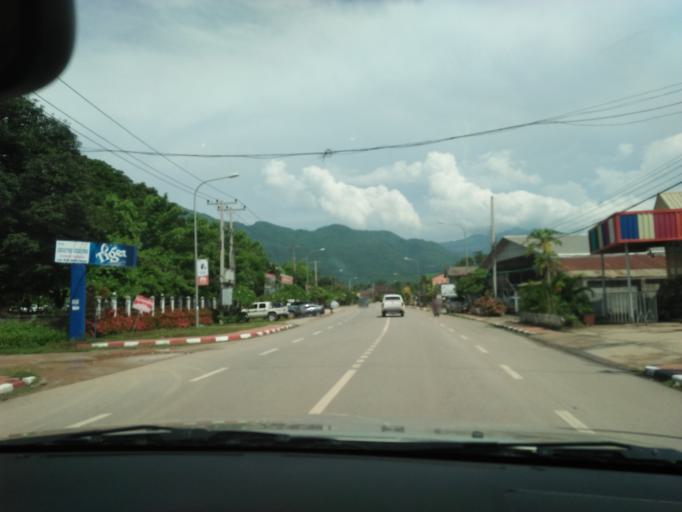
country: LA
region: Xiagnabouli
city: Sainyabuli
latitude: 19.2551
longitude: 101.7124
